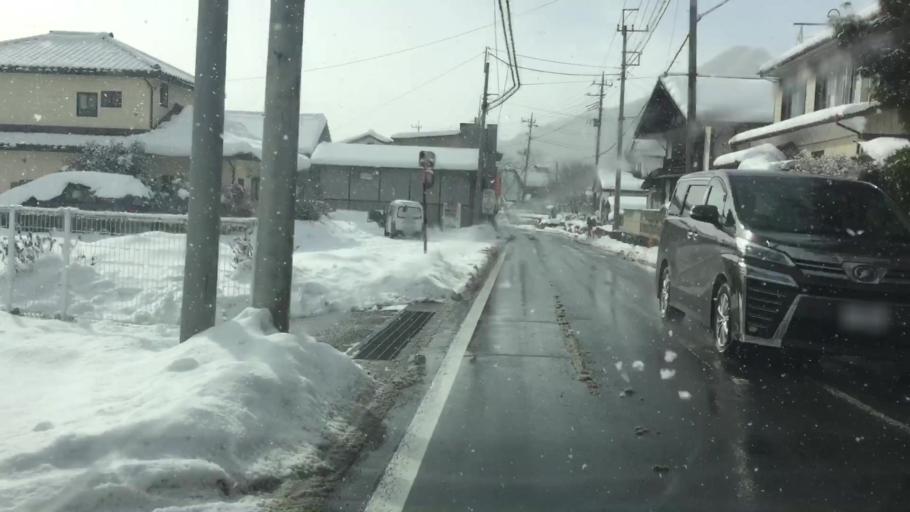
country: JP
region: Gunma
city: Numata
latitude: 36.6950
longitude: 139.0643
